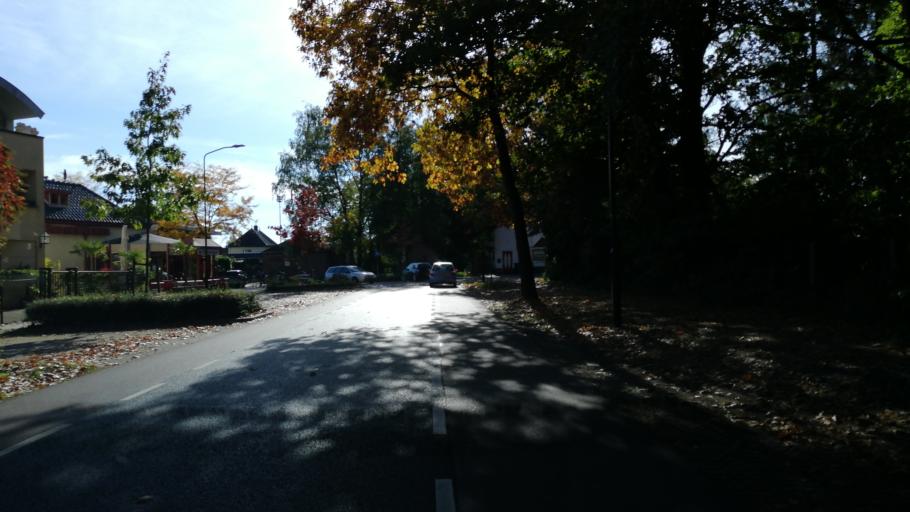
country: NL
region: Gelderland
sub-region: Gemeente Apeldoorn
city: Apeldoorn
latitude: 52.1992
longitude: 5.9492
